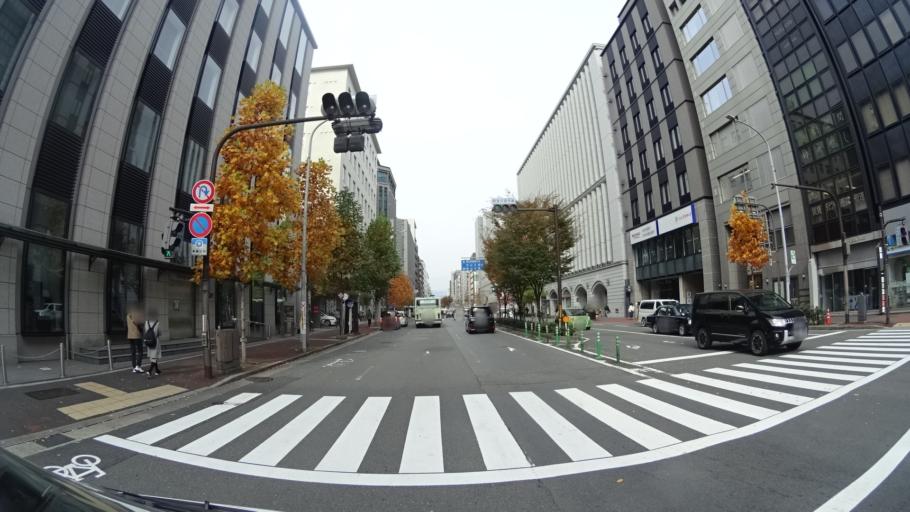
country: JP
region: Kyoto
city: Kyoto
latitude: 35.0028
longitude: 135.7597
